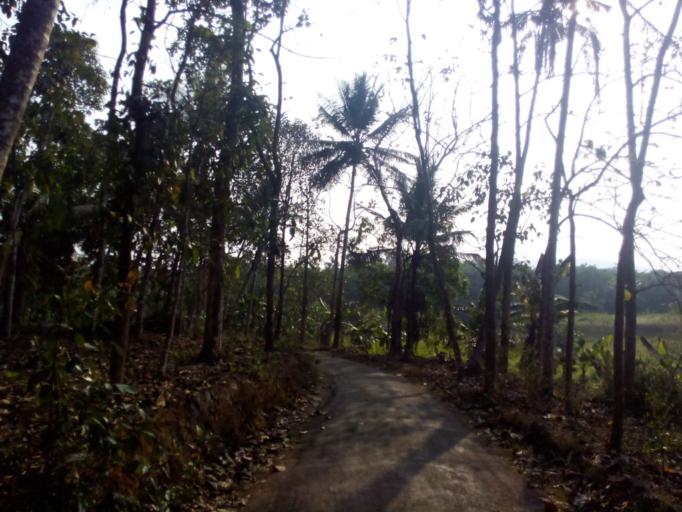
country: IN
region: Kerala
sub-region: Kottayam
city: Palackattumala
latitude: 9.7974
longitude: 76.6597
